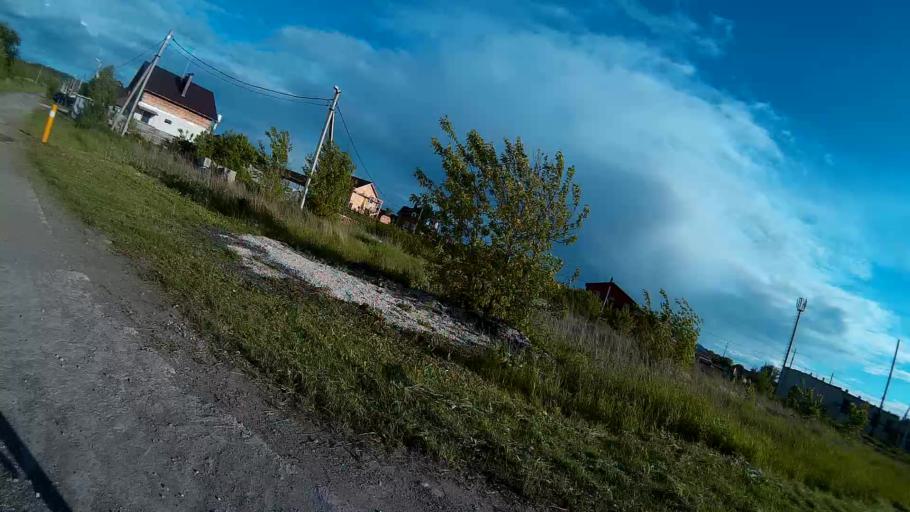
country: RU
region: Ulyanovsk
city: Novoul'yanovsk
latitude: 54.2050
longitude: 48.2711
